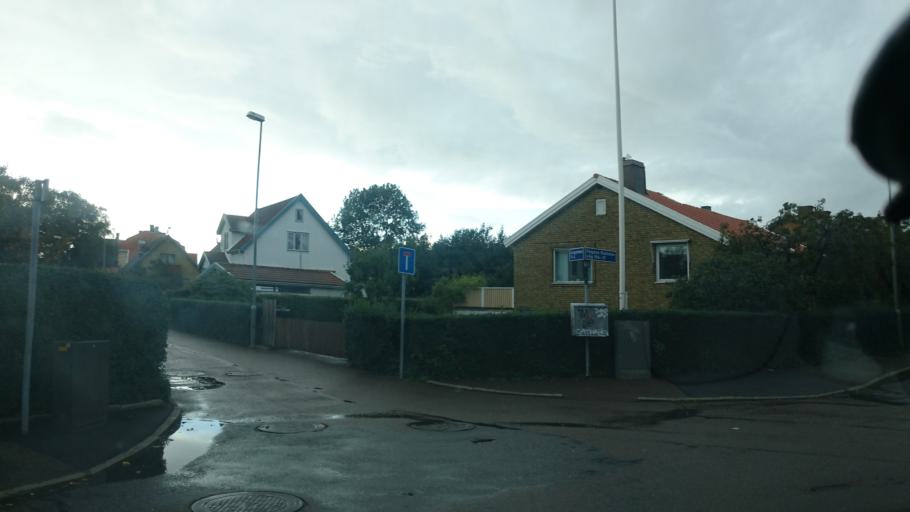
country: SE
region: Vaestra Goetaland
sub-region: Goteborg
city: Majorna
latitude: 57.6765
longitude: 11.8867
